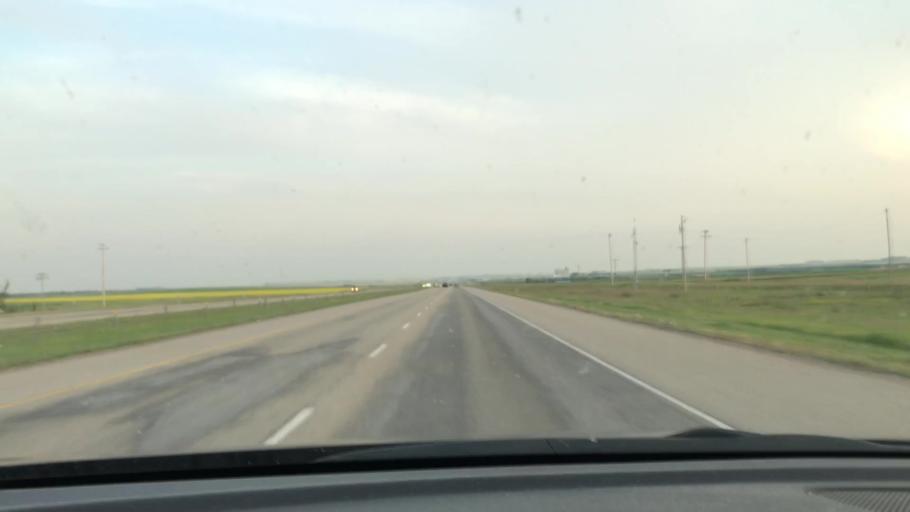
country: CA
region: Alberta
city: Carstairs
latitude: 51.5349
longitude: -114.0254
